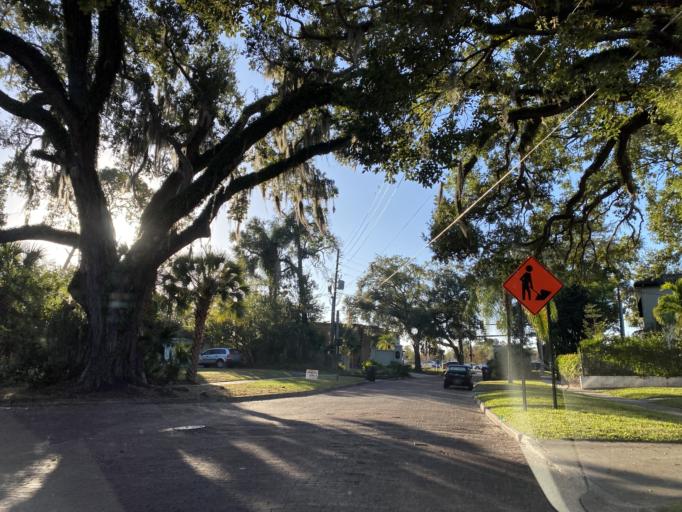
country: US
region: Florida
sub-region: Orange County
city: Orlando
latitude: 28.5538
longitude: -81.3976
